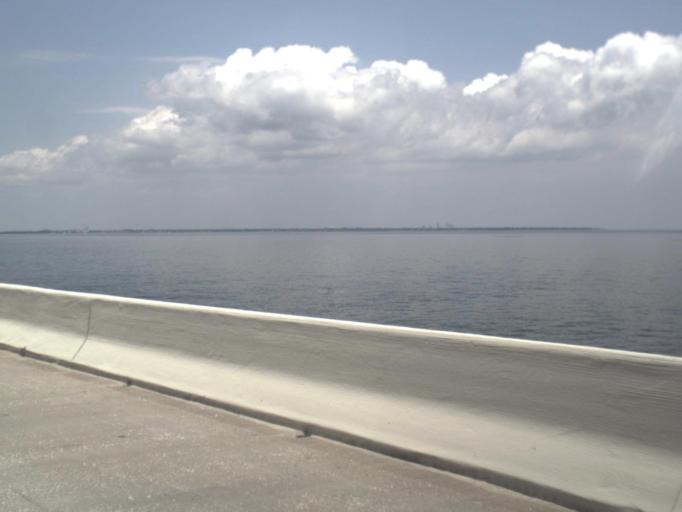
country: US
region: Florida
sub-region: Pinellas County
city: Tierra Verde
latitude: 27.6319
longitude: -82.6638
